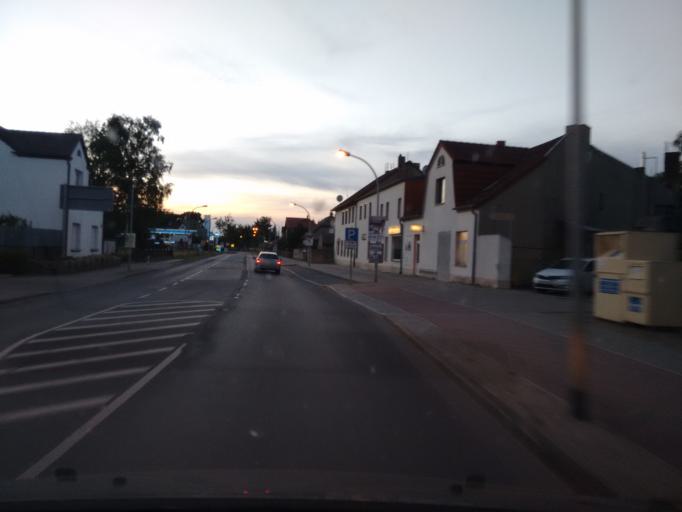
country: DE
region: Brandenburg
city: Storkow
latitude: 52.2621
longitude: 13.9372
